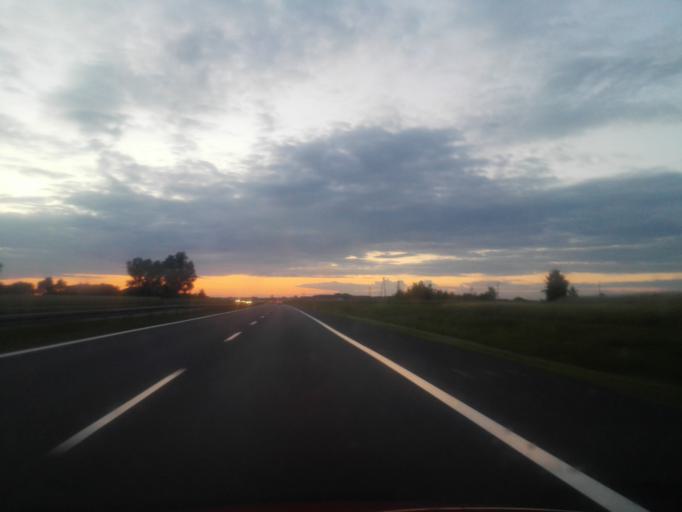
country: PL
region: Lodz Voivodeship
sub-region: Piotrkow Trybunalski
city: Piotrkow Trybunalski
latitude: 51.4652
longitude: 19.6357
